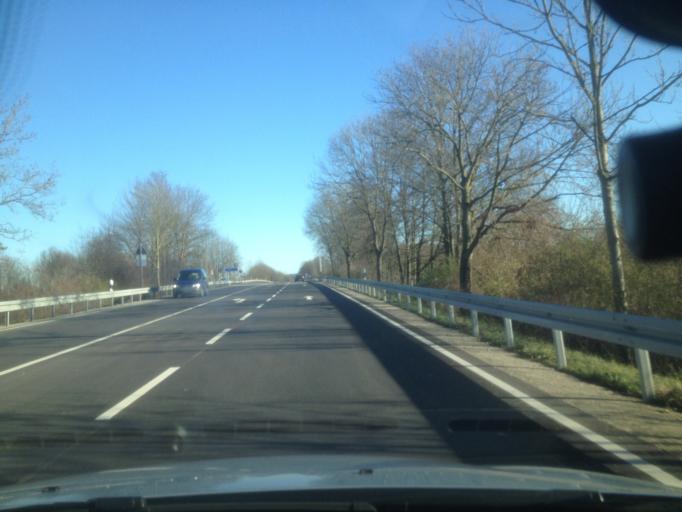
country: DE
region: Bavaria
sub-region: Upper Bavaria
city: Wang
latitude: 48.4802
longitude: 11.9890
